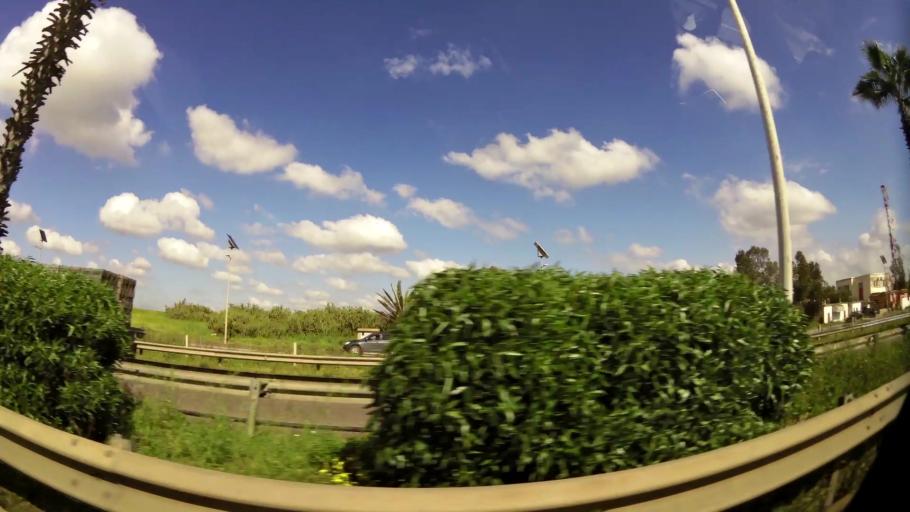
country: MA
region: Grand Casablanca
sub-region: Nouaceur
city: Bouskoura
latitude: 33.4199
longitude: -7.6270
